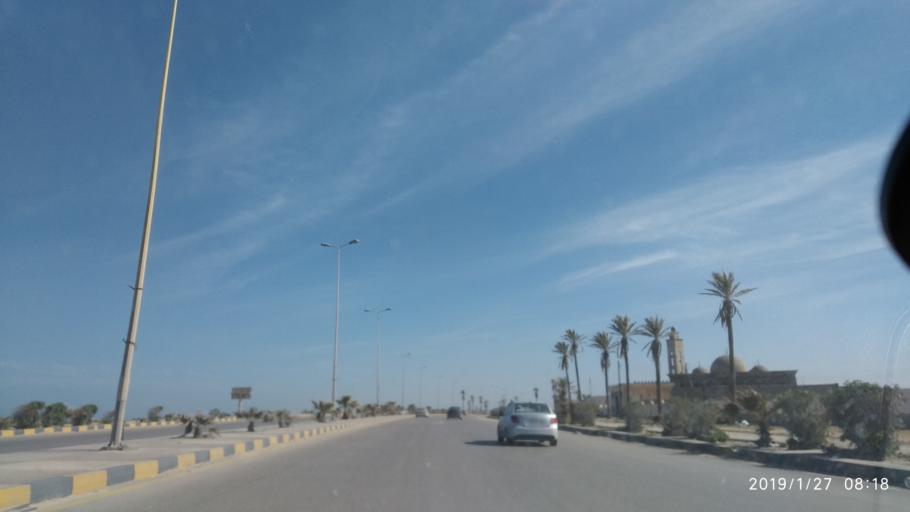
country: LY
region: Tripoli
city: Tagiura
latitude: 32.8951
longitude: 13.3358
